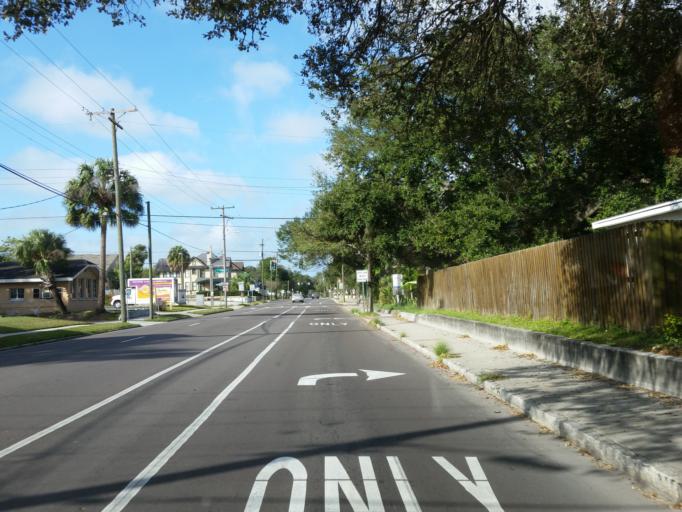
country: US
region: Florida
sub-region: Hillsborough County
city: Tampa
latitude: 27.9434
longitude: -82.4820
